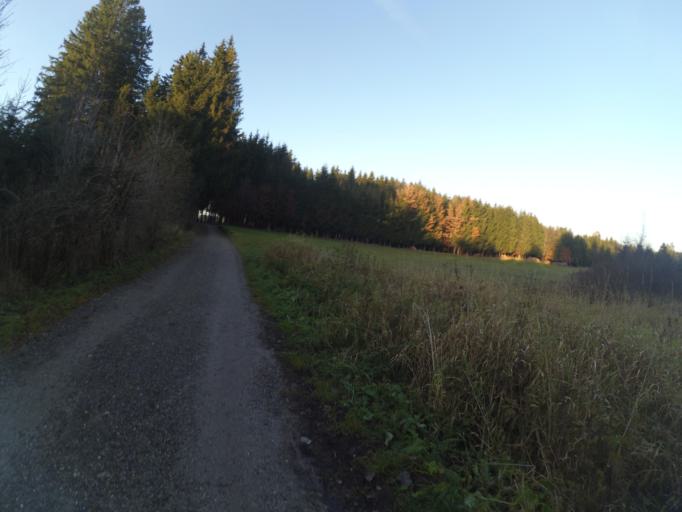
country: DE
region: Bavaria
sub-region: Swabia
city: Aitrang
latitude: 47.8010
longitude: 10.5427
